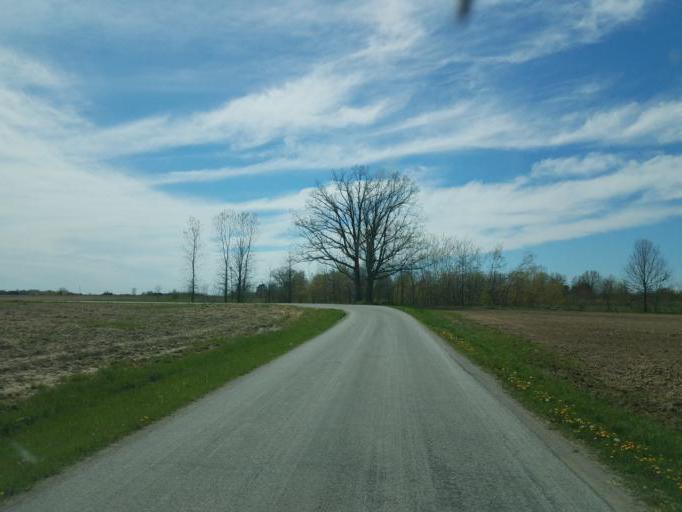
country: US
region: Ohio
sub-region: Huron County
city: Greenwich
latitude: 40.9095
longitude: -82.4676
